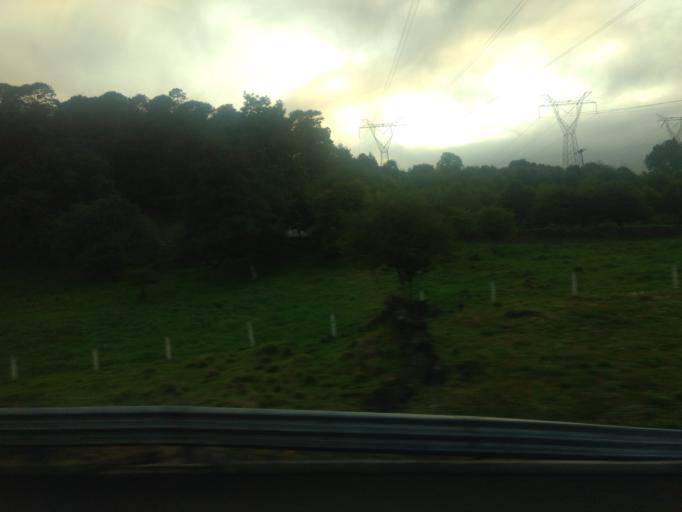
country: MX
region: Veracruz
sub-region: Acajete
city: La Joya
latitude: 19.6301
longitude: -97.0280
